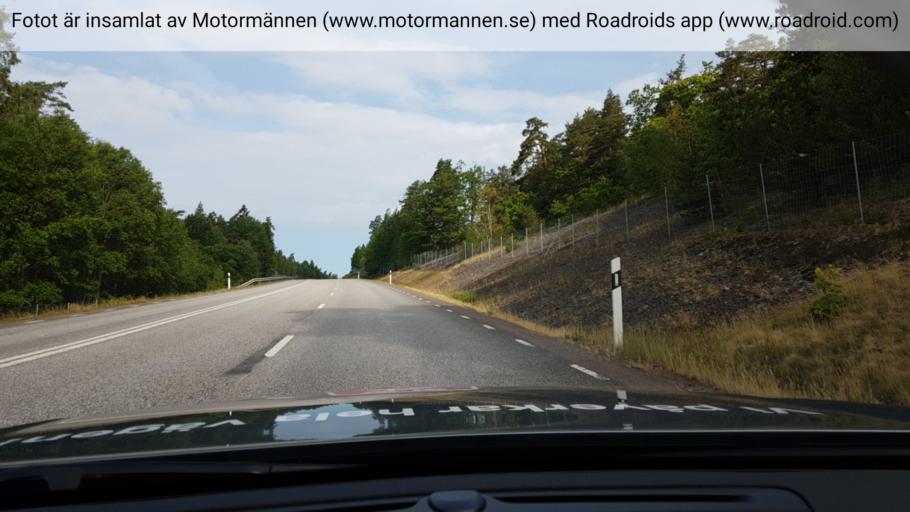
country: SE
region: OEstergoetland
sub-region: Motala Kommun
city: Borensberg
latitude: 58.5617
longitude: 15.3135
